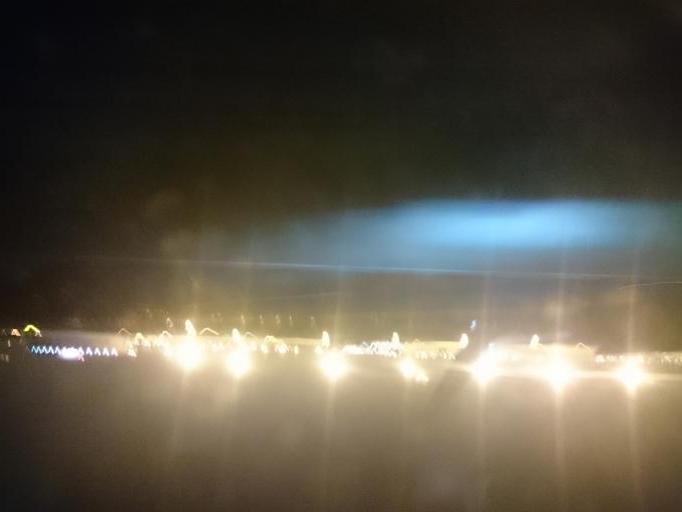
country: ES
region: Catalonia
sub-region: Provincia de Barcelona
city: El Prat de Llobregat
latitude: 41.3015
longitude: 2.0915
